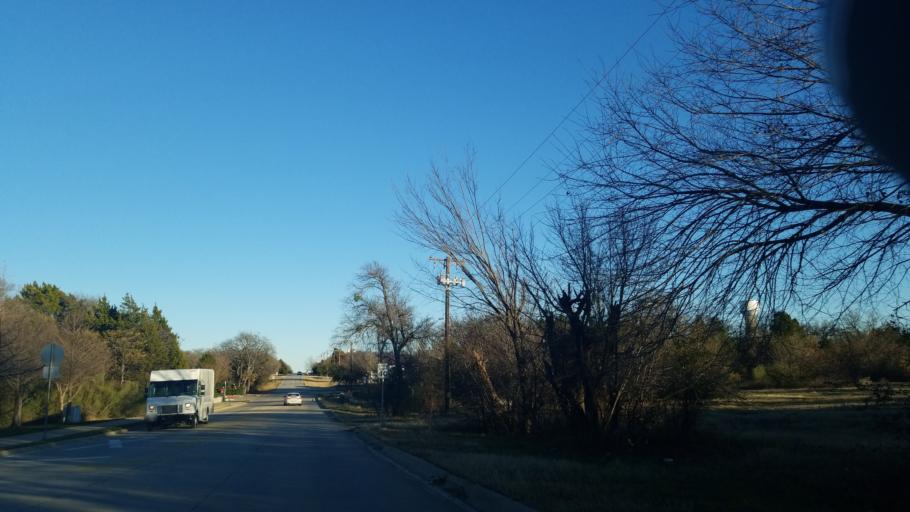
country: US
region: Texas
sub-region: Denton County
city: Corinth
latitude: 33.1632
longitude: -97.0680
